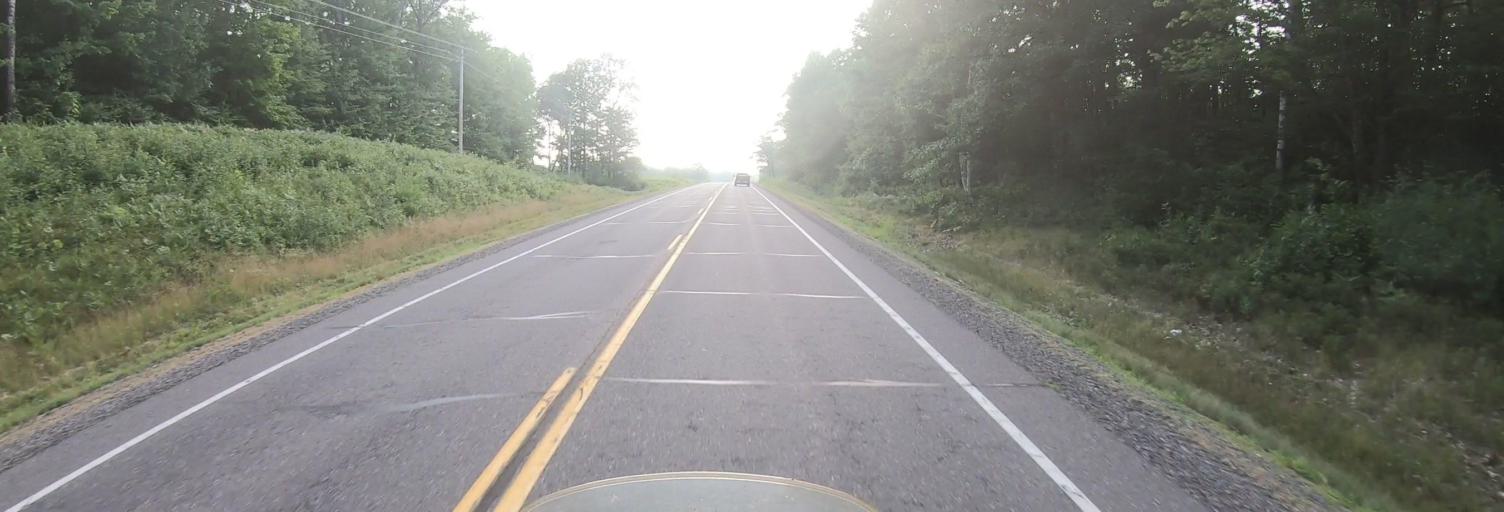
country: US
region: Wisconsin
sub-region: Sawyer County
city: Little Round Lake
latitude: 46.0644
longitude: -91.1474
